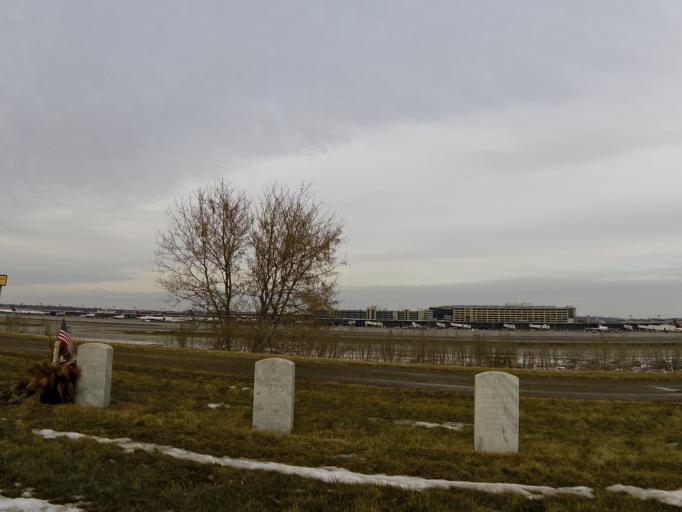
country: US
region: Minnesota
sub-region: Hennepin County
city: Richfield
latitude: 44.8755
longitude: -93.2137
